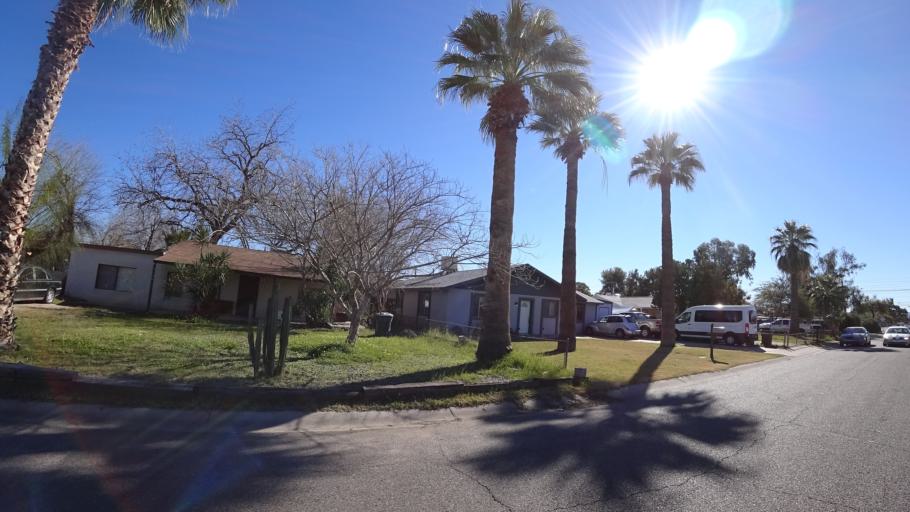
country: US
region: Arizona
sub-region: Maricopa County
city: Phoenix
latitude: 33.5030
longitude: -112.0520
